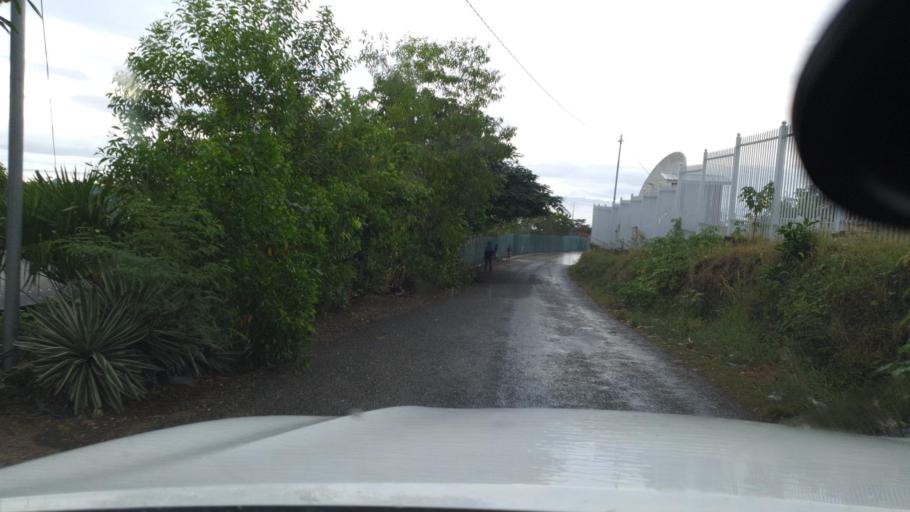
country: SB
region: Guadalcanal
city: Honiara
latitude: -9.4394
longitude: 159.9506
